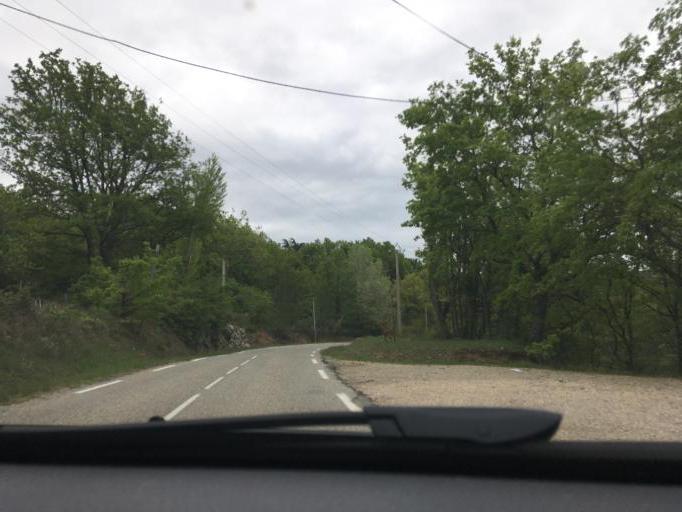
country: FR
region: Provence-Alpes-Cote d'Azur
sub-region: Departement du Var
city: Regusse
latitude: 43.7149
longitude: 6.1929
